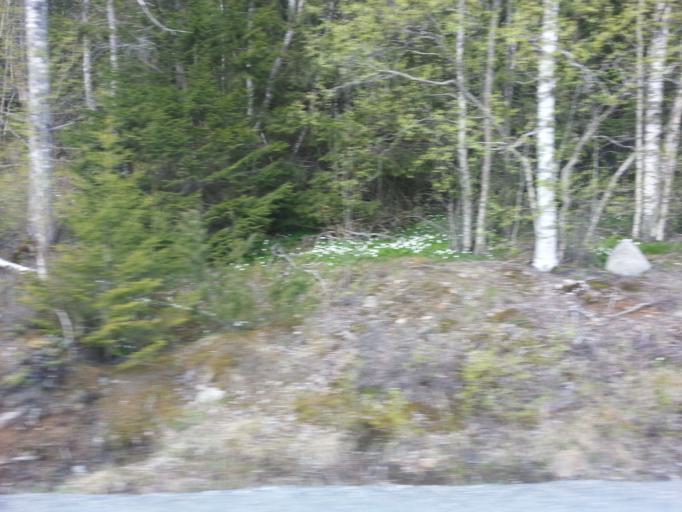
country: NO
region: Nord-Trondelag
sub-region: Levanger
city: Skogn
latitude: 63.6322
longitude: 11.2119
